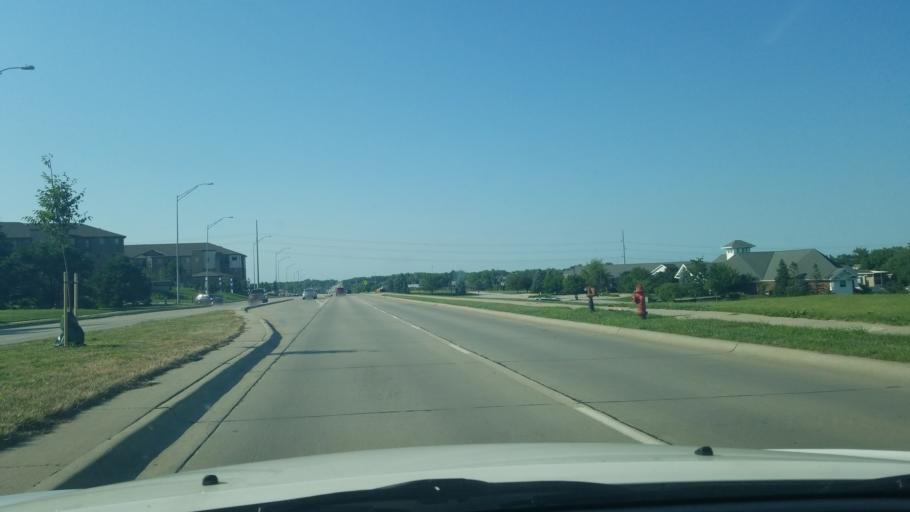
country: US
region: Nebraska
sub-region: Lancaster County
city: Lincoln
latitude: 40.7490
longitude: -96.6061
